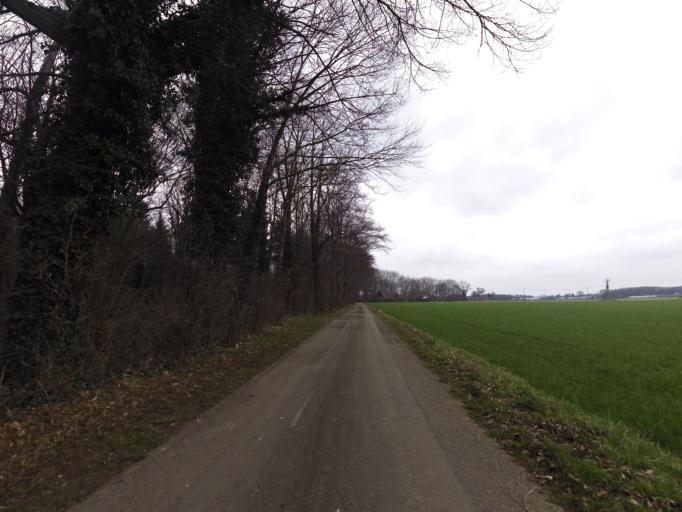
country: NL
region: Gelderland
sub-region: Oude IJsselstreek
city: Gendringen
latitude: 51.8692
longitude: 6.4015
